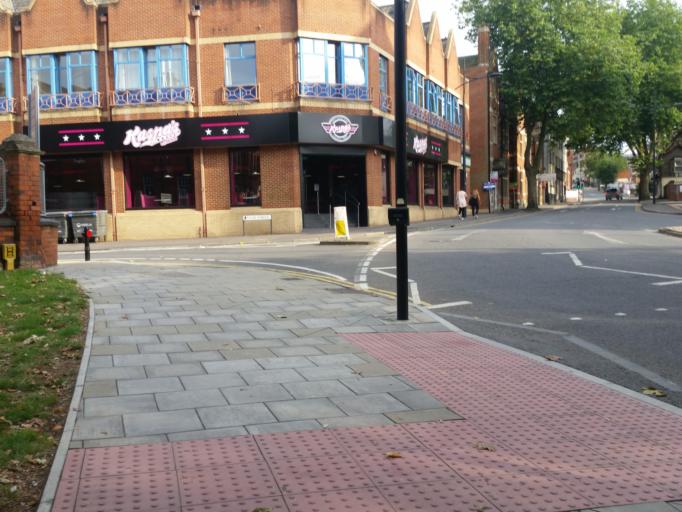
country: GB
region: England
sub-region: Borough of Swindon
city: Swindon
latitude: 51.5595
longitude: -1.7800
